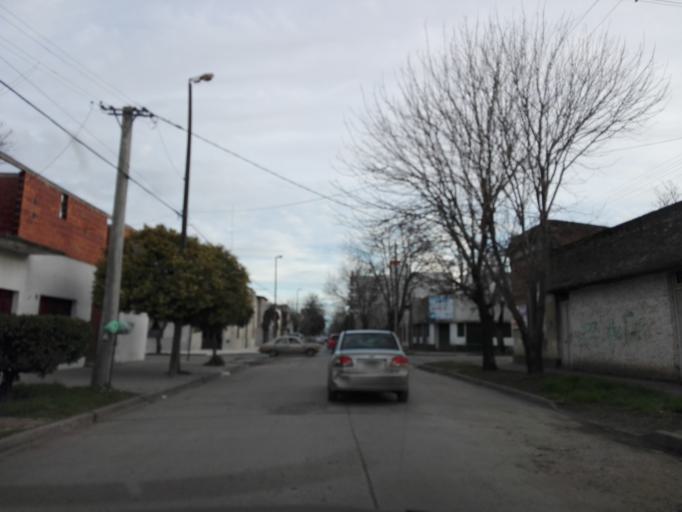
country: AR
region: Buenos Aires
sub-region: Partido de Balcarce
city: Balcarce
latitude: -37.8454
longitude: -58.2502
